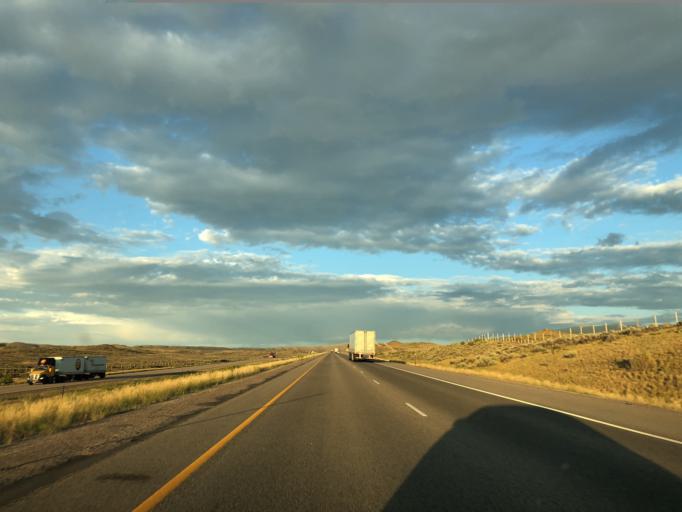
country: US
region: Wyoming
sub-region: Carbon County
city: Saratoga
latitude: 41.7328
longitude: -106.7204
